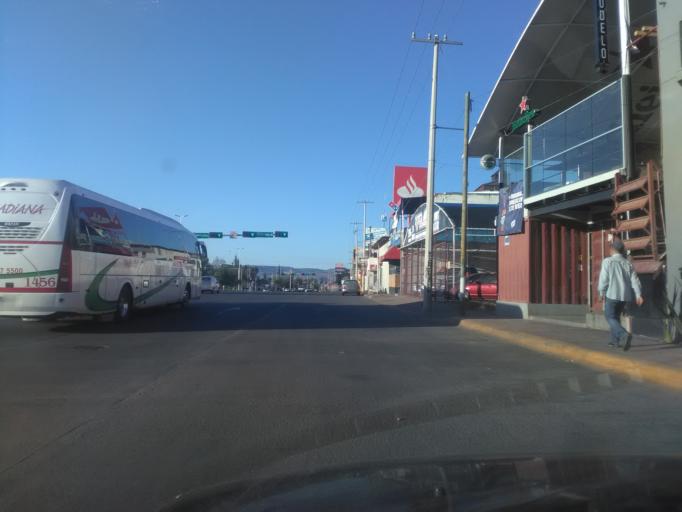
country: MX
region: Durango
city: Victoria de Durango
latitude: 24.0191
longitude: -104.6902
